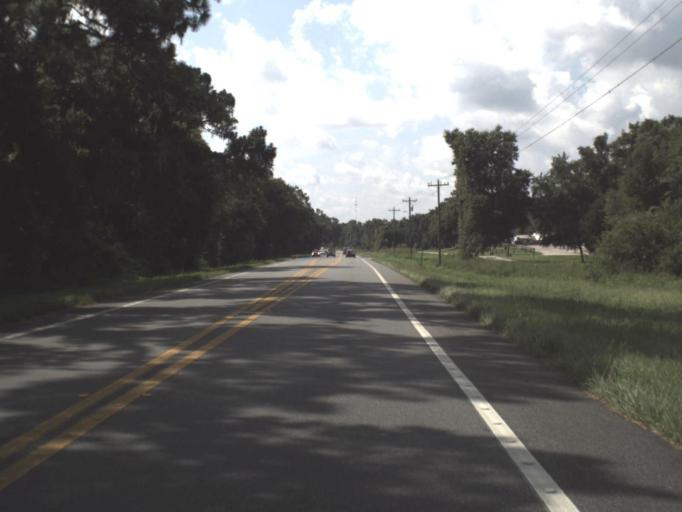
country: US
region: Florida
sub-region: Citrus County
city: Inverness Highlands North
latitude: 28.8710
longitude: -82.3610
